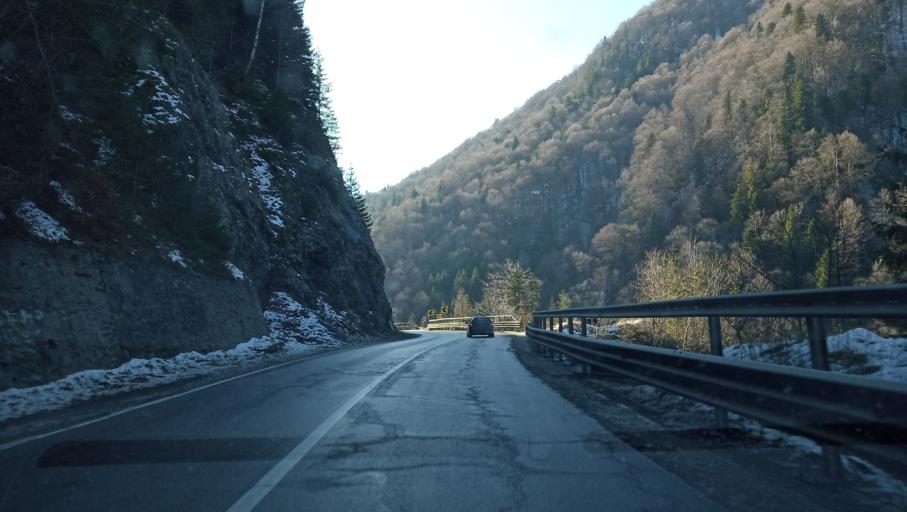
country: RO
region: Brasov
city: Crivina
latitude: 45.4730
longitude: 25.9211
